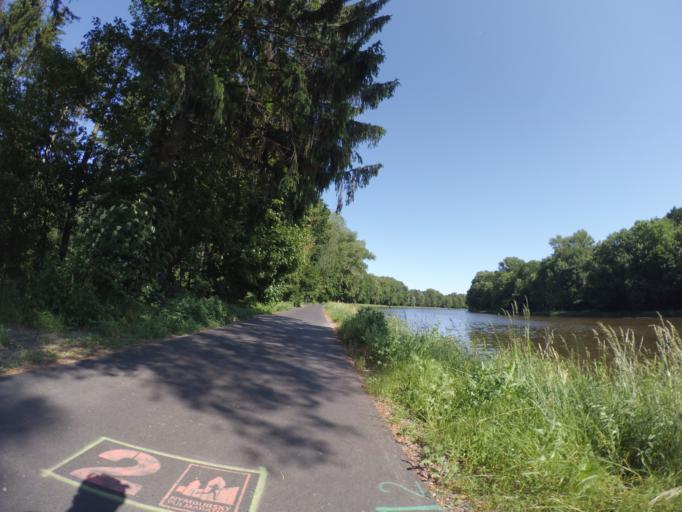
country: CZ
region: Central Bohemia
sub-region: Okres Nymburk
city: Nymburk
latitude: 50.1799
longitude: 15.0690
